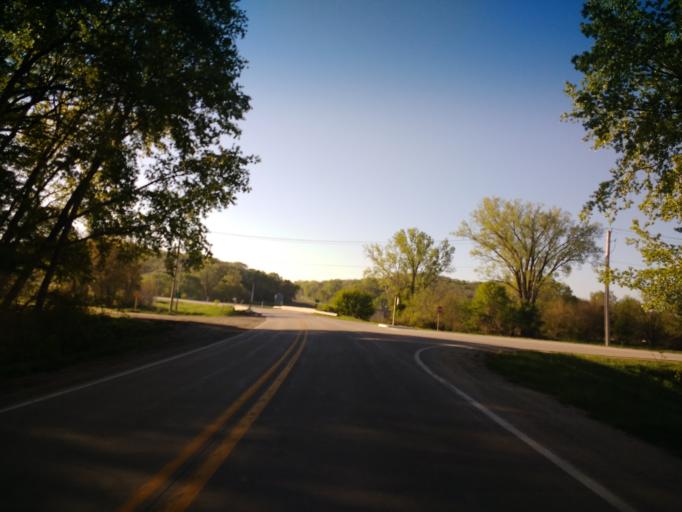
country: US
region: Iowa
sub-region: Harrison County
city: Missouri Valley
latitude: 41.4343
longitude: -95.8683
